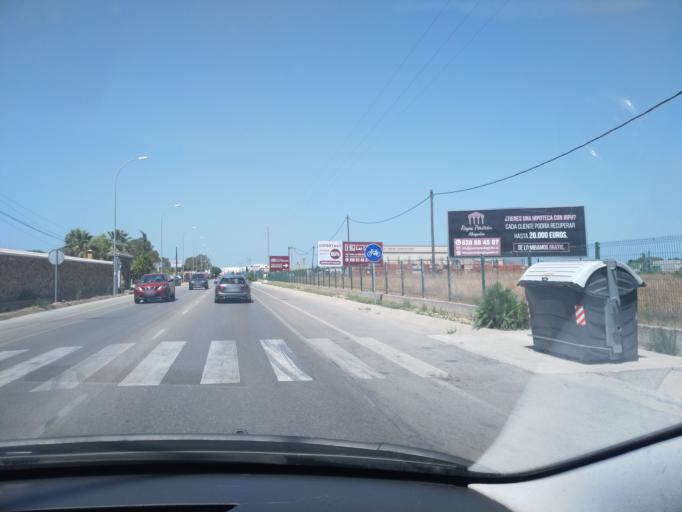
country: ES
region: Andalusia
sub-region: Provincia de Cadiz
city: Chiclana de la Frontera
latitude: 36.3952
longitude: -6.1602
